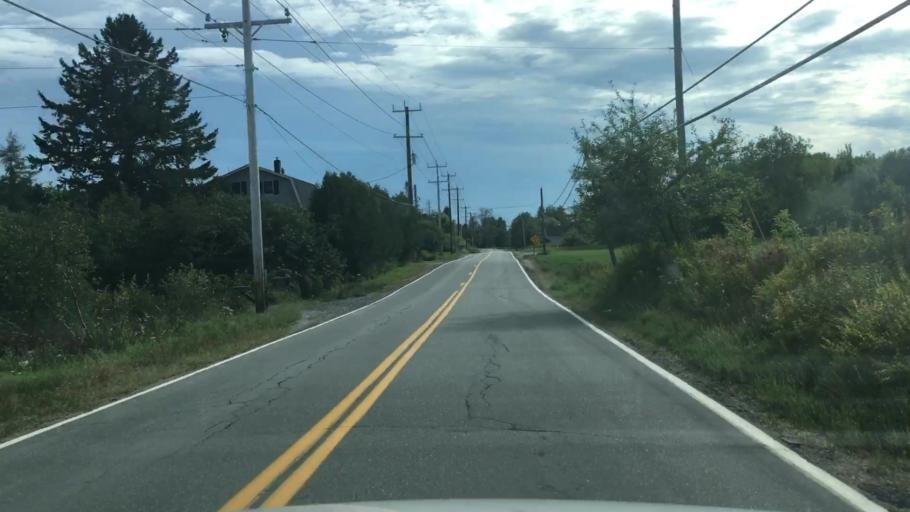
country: US
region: Maine
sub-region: Hancock County
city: Ellsworth
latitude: 44.5032
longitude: -68.4190
